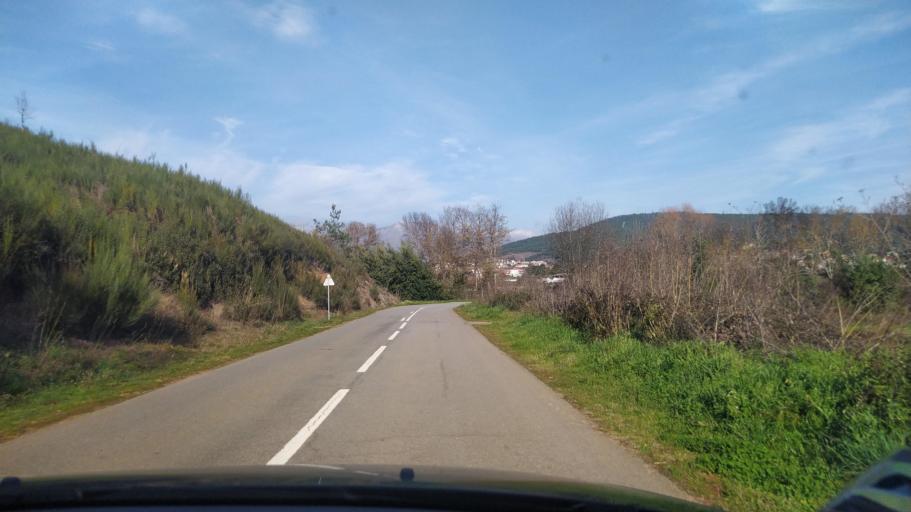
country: PT
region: Castelo Branco
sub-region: Concelho do Fundao
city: Aldeia de Joanes
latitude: 40.1873
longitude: -7.6434
